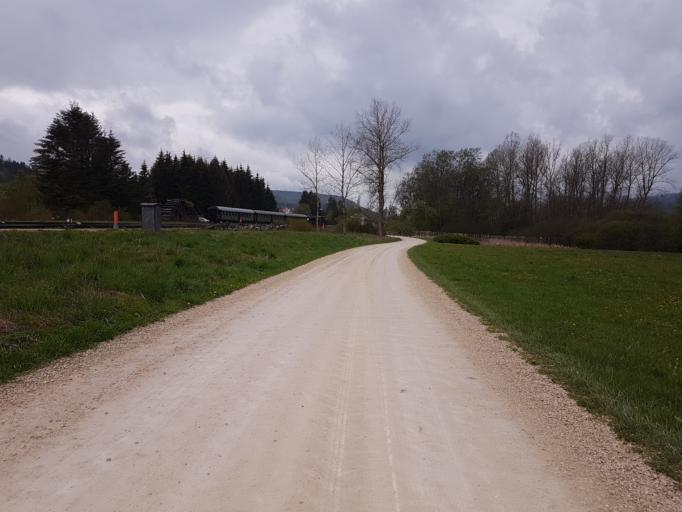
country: DE
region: Baden-Wuerttemberg
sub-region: Freiburg Region
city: Blumberg
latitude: 47.8381
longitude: 8.5624
